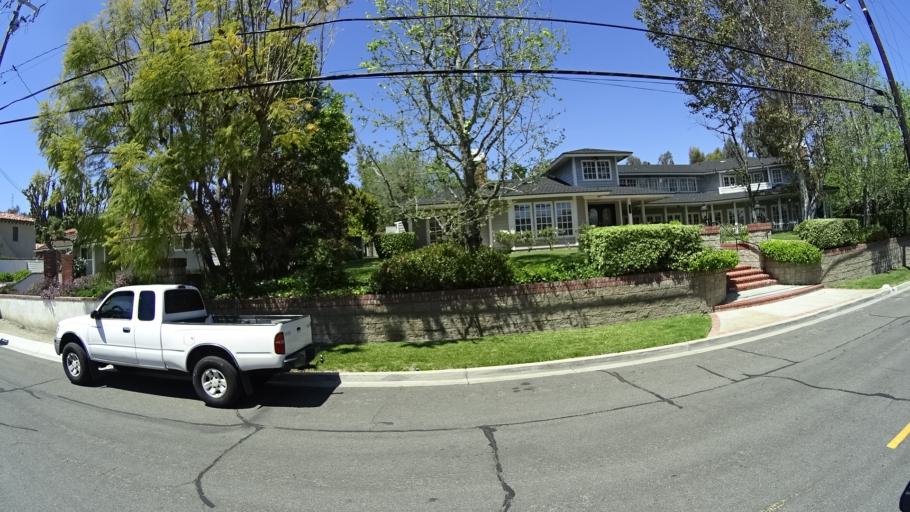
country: US
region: California
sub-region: Orange County
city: Villa Park
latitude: 33.8271
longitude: -117.8010
